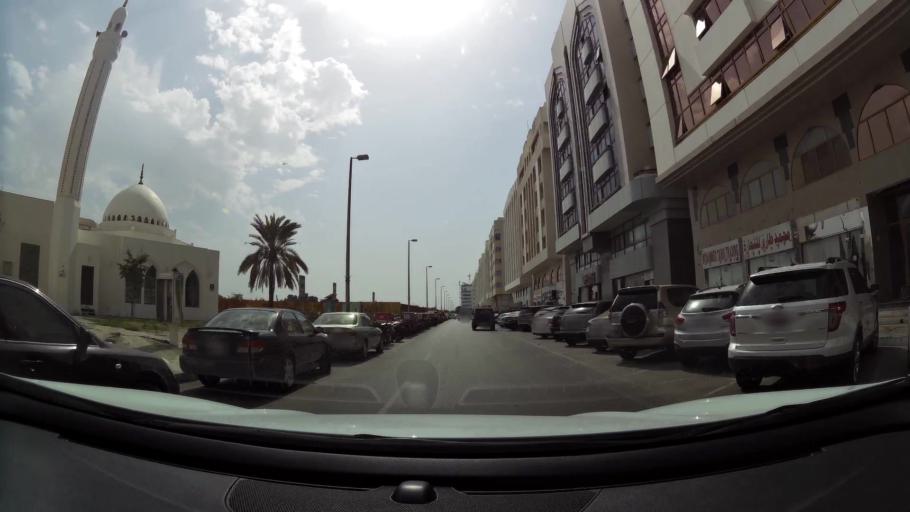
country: AE
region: Abu Dhabi
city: Abu Dhabi
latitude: 24.4791
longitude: 54.3599
